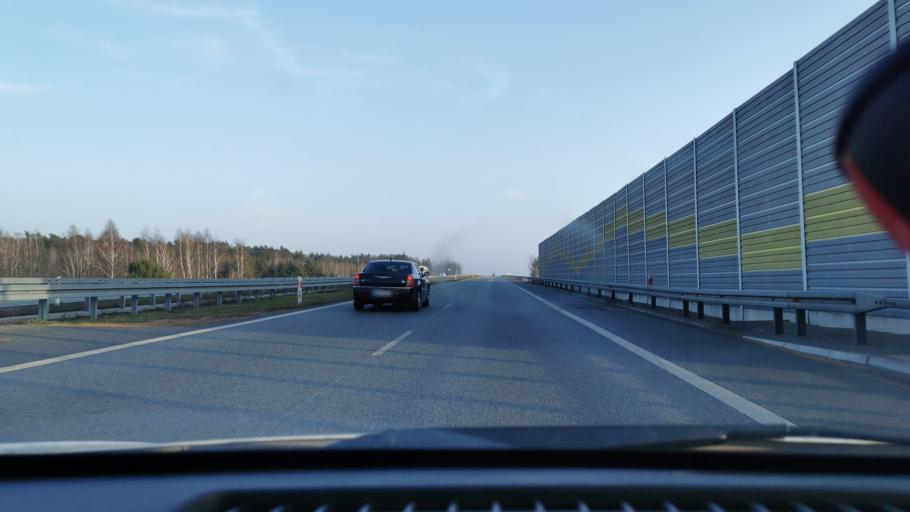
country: PL
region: Lodz Voivodeship
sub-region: Powiat zdunskowolski
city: Zdunska Wola
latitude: 51.5682
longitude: 18.9745
